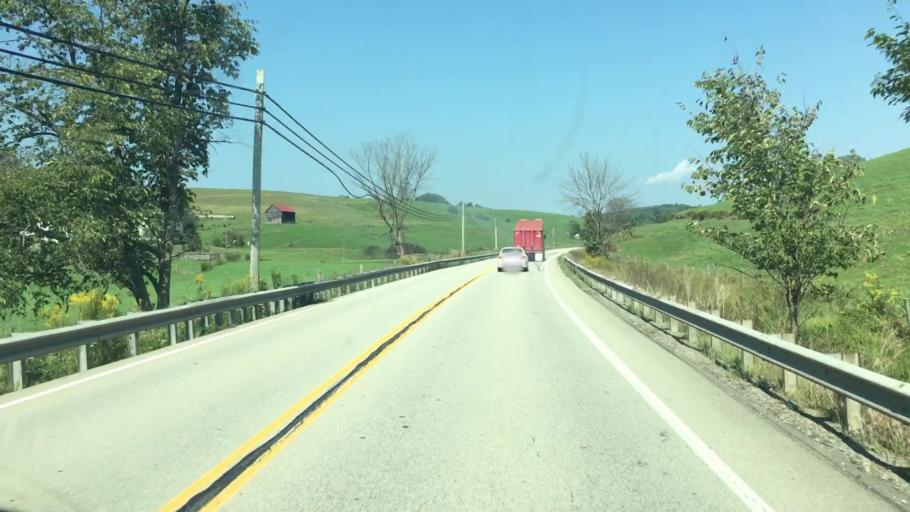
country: US
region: Pennsylvania
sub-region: Washington County
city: Washington
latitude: 40.0602
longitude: -80.2985
